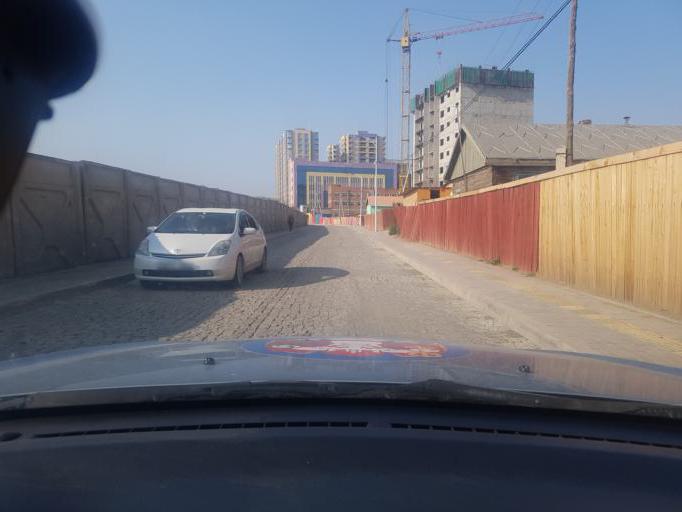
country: MN
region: Ulaanbaatar
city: Ulaanbaatar
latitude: 47.9218
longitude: 106.9665
